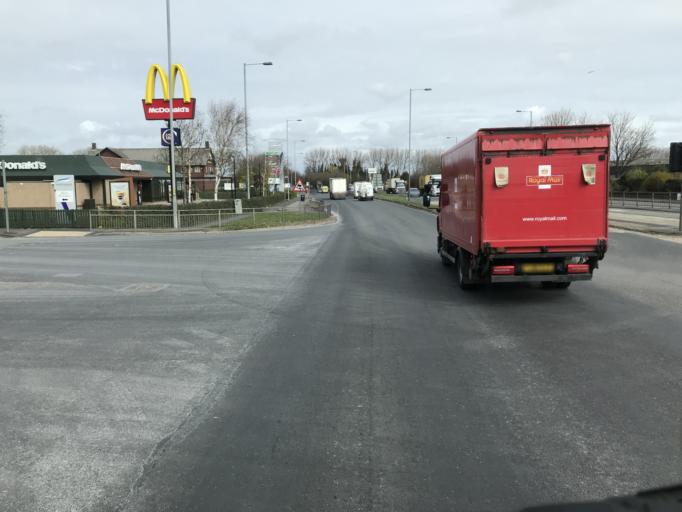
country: GB
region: England
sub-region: Sefton
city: Litherland
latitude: 53.4838
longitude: -2.9627
